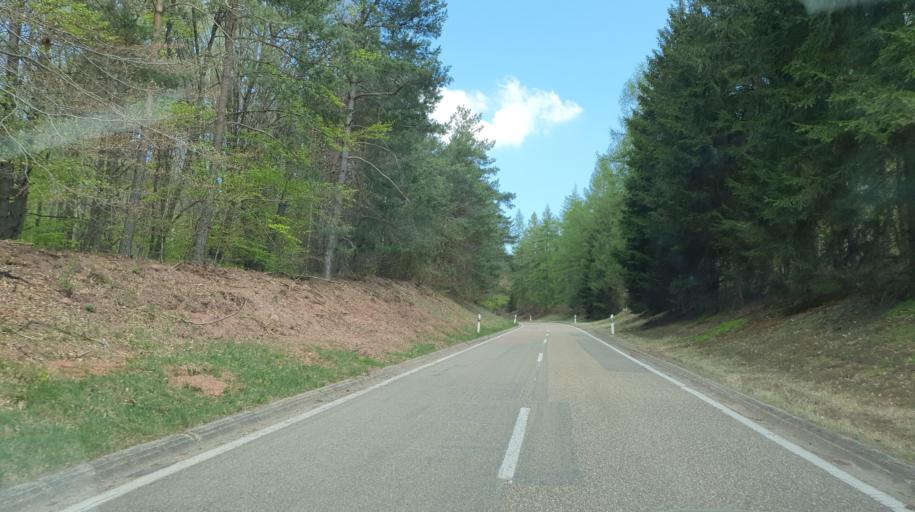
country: DE
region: Rheinland-Pfalz
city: Hauenstein
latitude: 49.2184
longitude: 7.8360
